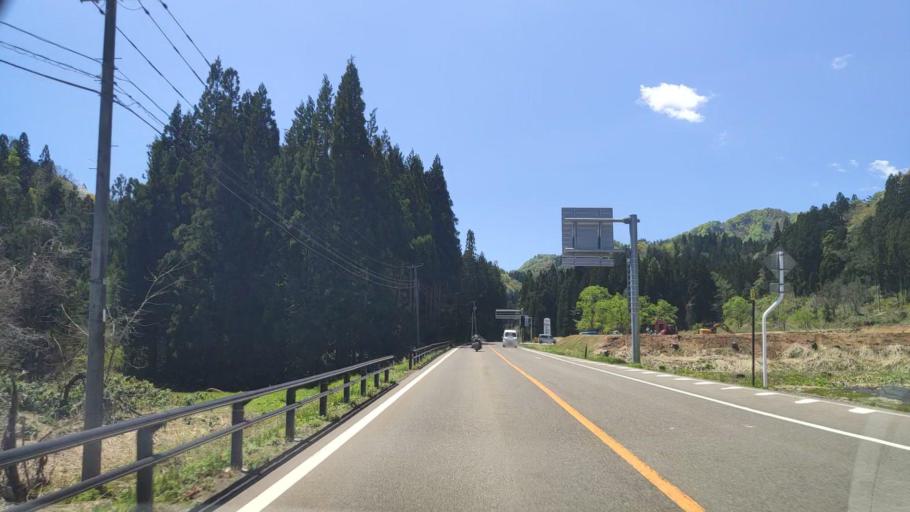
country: JP
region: Akita
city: Yuzawa
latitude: 39.0368
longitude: 140.3897
